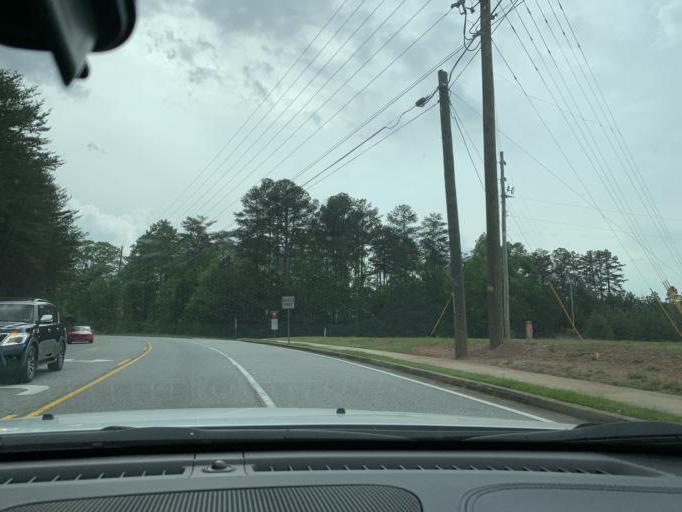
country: US
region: Georgia
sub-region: Gwinnett County
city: Sugar Hill
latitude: 34.1219
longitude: -84.1066
